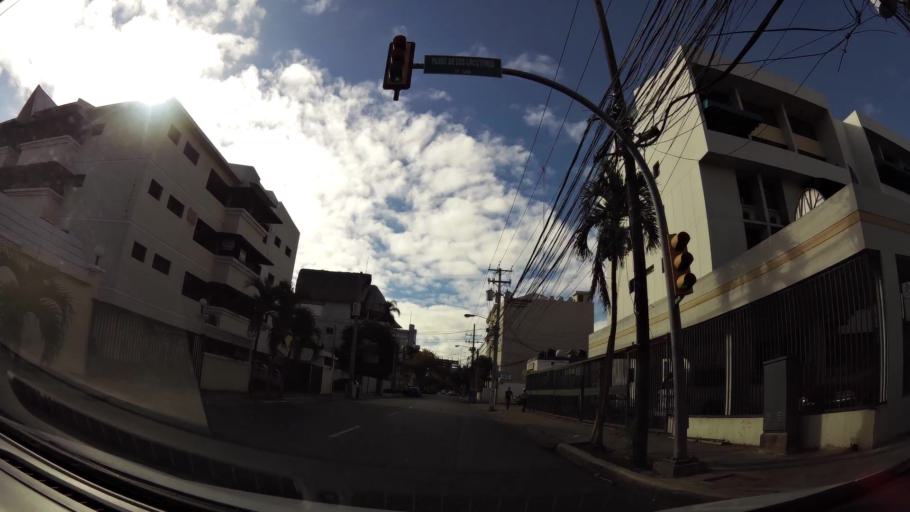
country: DO
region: Nacional
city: La Julia
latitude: 18.4661
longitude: -69.9356
